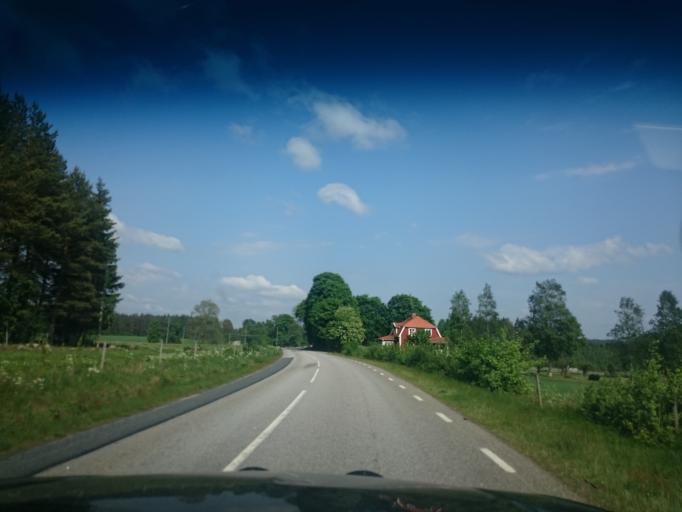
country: SE
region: Joenkoeping
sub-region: Vetlanda Kommun
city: Vetlanda
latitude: 57.3791
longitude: 14.9976
